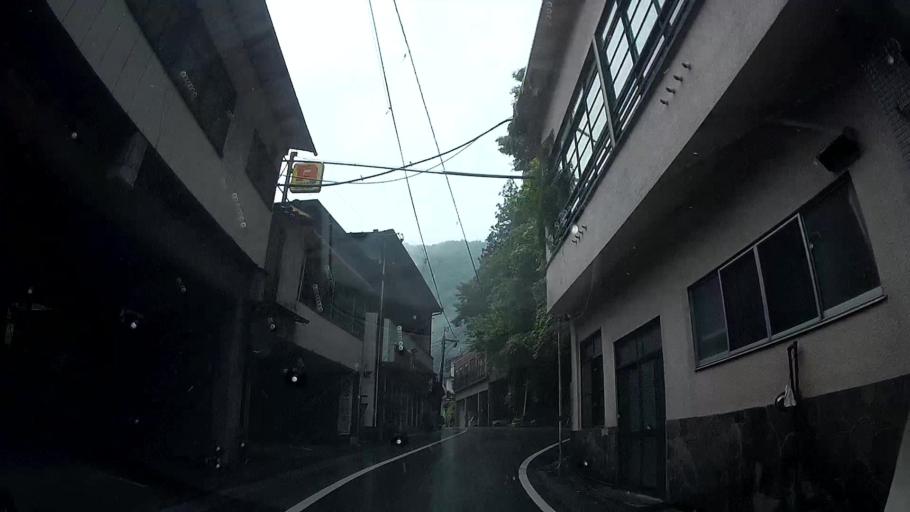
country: JP
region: Oita
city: Tsukawaki
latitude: 33.1846
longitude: 131.0326
